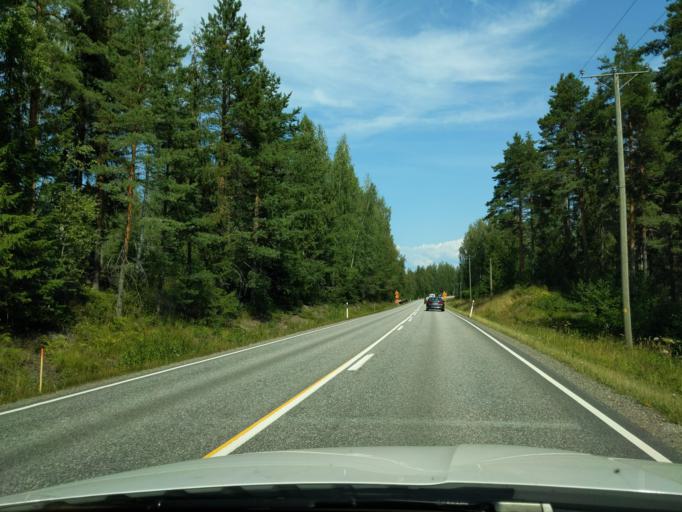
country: FI
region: Paijanne Tavastia
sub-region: Lahti
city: Padasjoki
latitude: 61.3329
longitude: 25.2164
